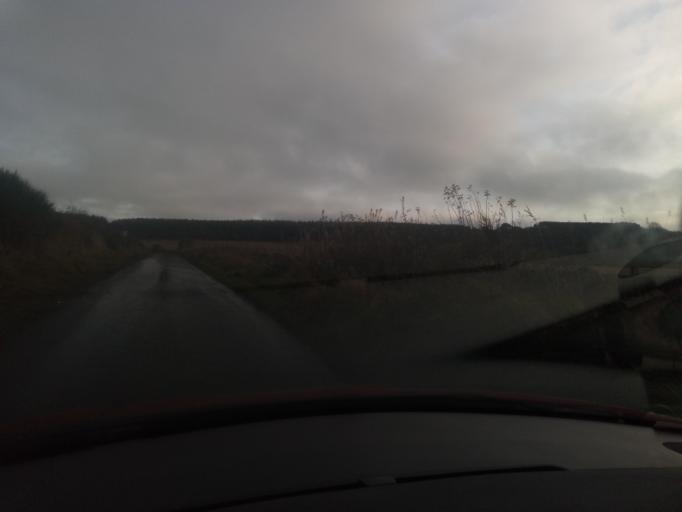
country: GB
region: Scotland
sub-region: The Scottish Borders
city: Jedburgh
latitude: 55.4878
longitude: -2.5973
